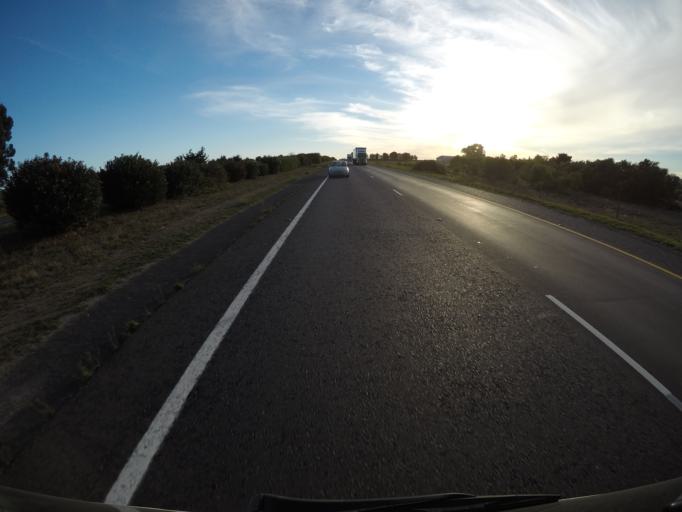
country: ZA
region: Western Cape
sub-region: City of Cape Town
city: Kraaifontein
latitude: -33.8222
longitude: 18.7829
